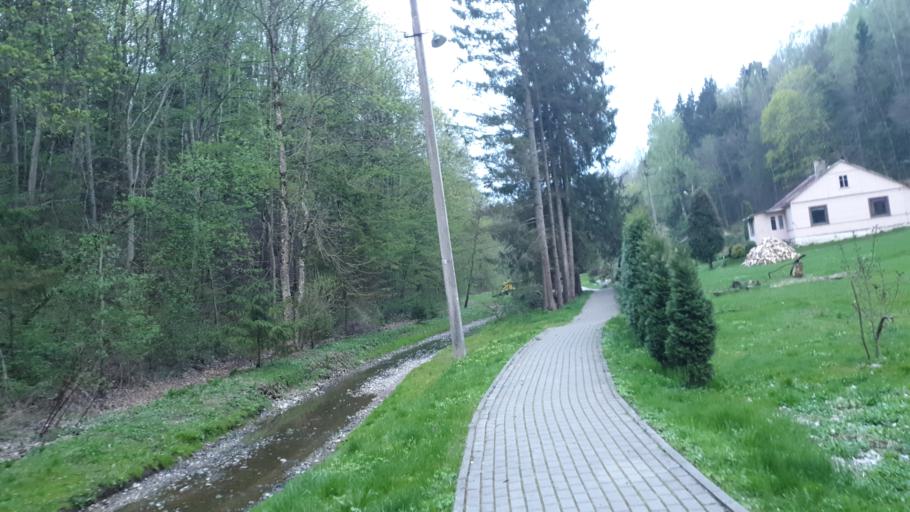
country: LT
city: Sakiai
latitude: 55.0809
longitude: 23.1783
